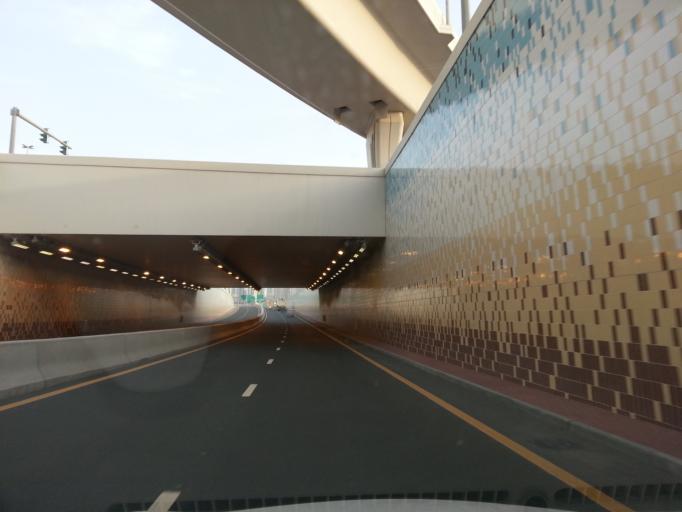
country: AE
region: Dubai
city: Dubai
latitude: 25.0570
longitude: 55.1394
